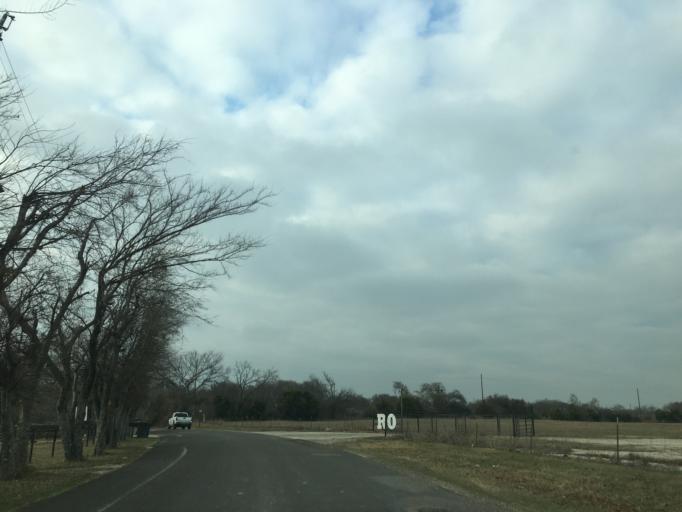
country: US
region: Texas
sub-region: Ellis County
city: Red Oak
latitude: 32.4936
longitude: -96.8032
